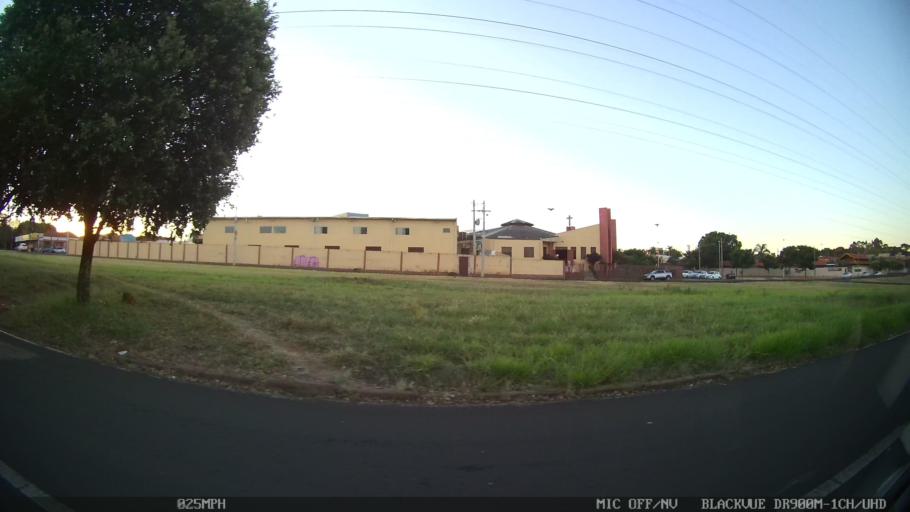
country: BR
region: Sao Paulo
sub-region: Sao Jose Do Rio Preto
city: Sao Jose do Rio Preto
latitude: -20.8440
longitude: -49.3783
